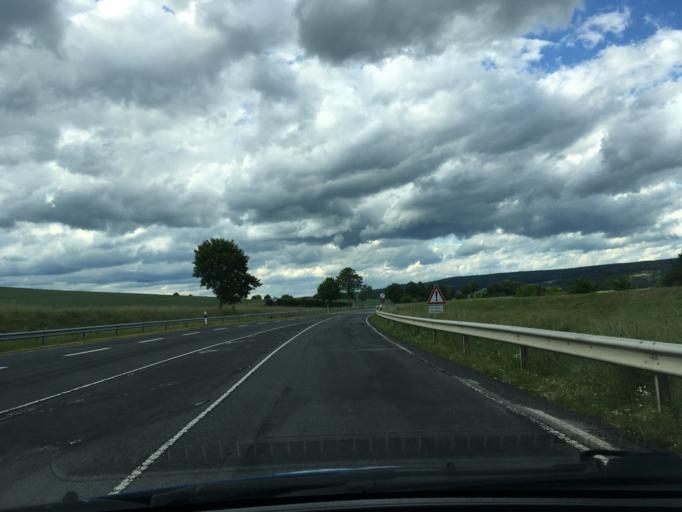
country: DE
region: Lower Saxony
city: Einbeck
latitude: 51.7852
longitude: 9.8990
